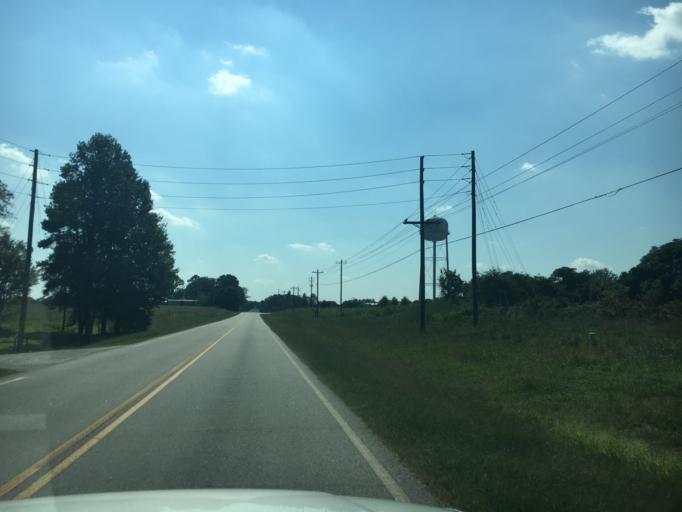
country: US
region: Georgia
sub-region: Franklin County
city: Gumlog
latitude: 34.4668
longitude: -83.0614
